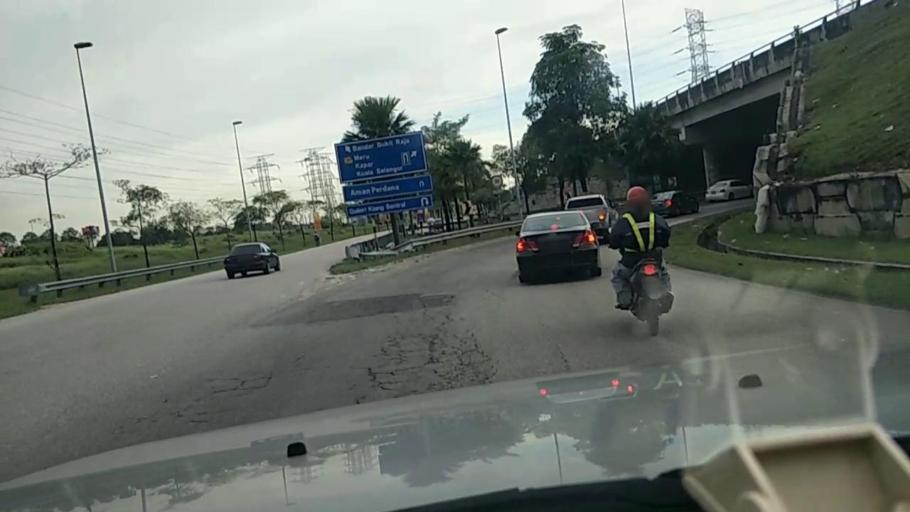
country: MY
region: Selangor
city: Klang
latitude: 3.1074
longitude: 101.4427
